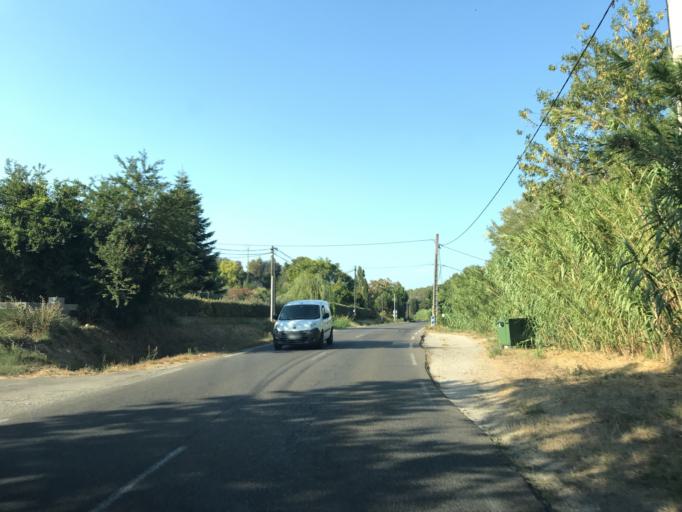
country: FR
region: Provence-Alpes-Cote d'Azur
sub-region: Departement des Bouches-du-Rhone
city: Saint-Chamas
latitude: 43.5590
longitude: 5.0146
